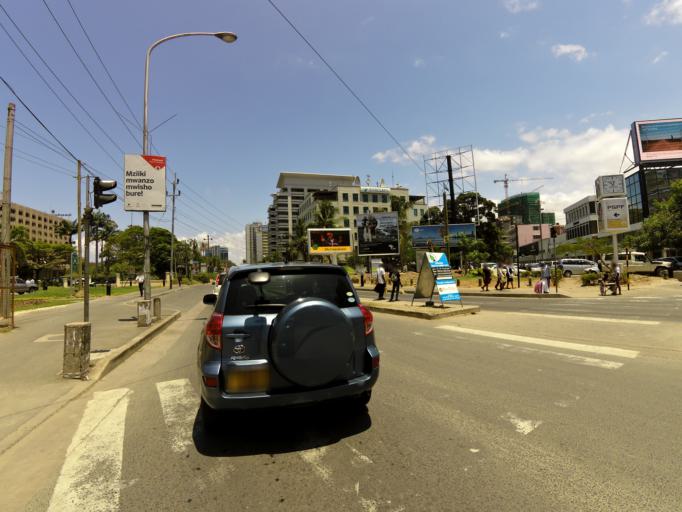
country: TZ
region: Dar es Salaam
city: Dar es Salaam
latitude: -6.8102
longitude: 39.2869
